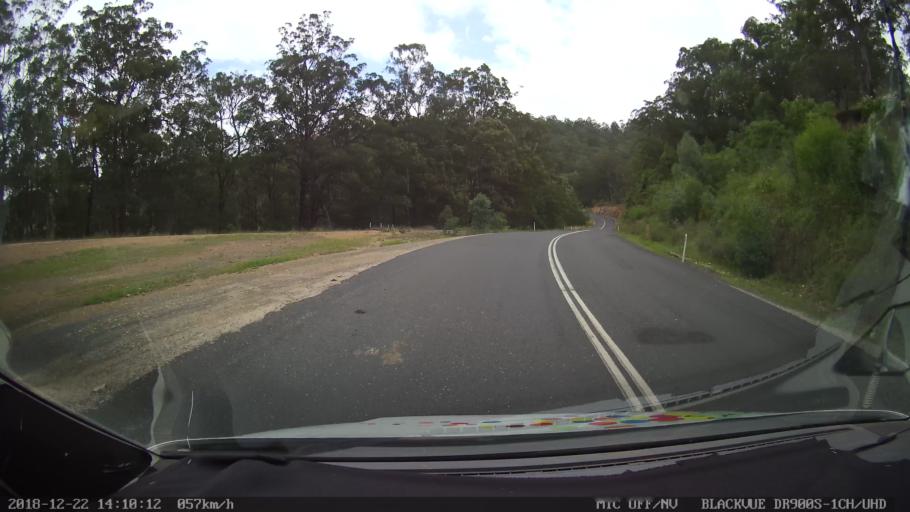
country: AU
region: New South Wales
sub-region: Clarence Valley
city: Coutts Crossing
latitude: -29.9913
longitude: 152.7113
